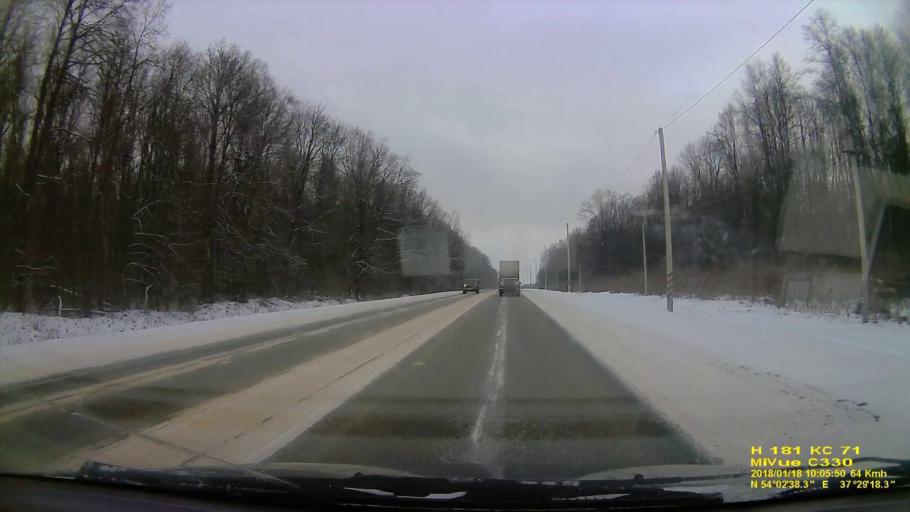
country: RU
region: Tula
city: Pervomayskiy
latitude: 54.0438
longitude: 37.4884
